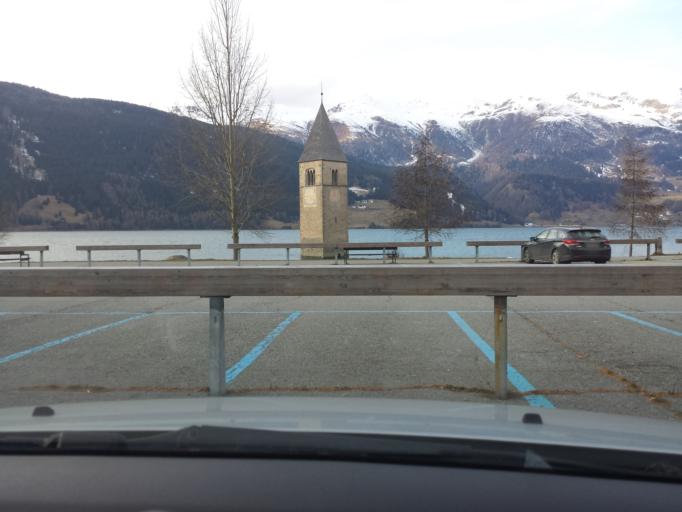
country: IT
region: Trentino-Alto Adige
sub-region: Bolzano
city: Curon Venosta
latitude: 46.8105
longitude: 10.5382
